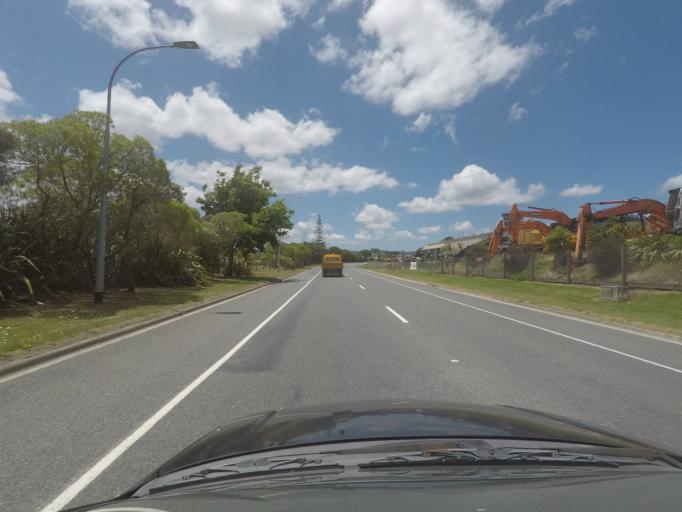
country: NZ
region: Northland
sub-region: Whangarei
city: Whangarei
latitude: -35.7452
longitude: 174.3239
